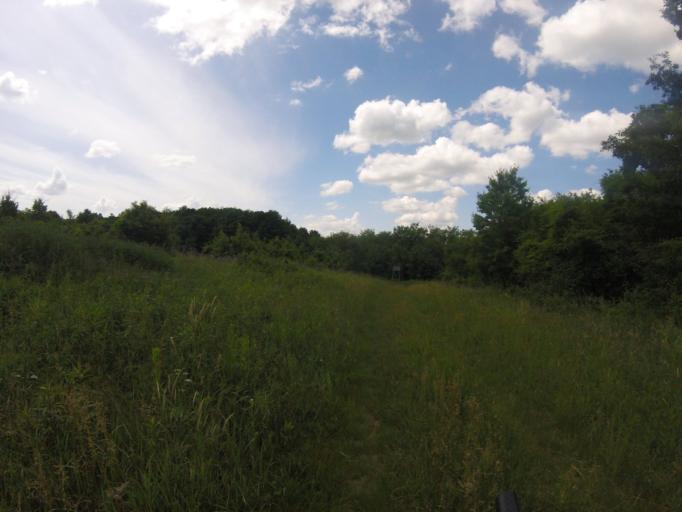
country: HU
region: Zala
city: Zalaszentgrot
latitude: 46.8965
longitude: 17.0340
